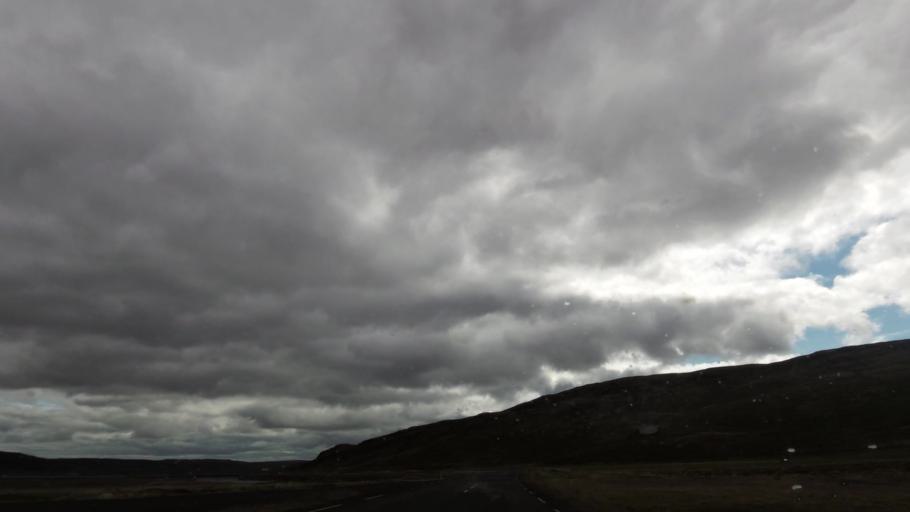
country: IS
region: West
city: Stykkisholmur
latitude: 65.7674
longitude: -21.7936
